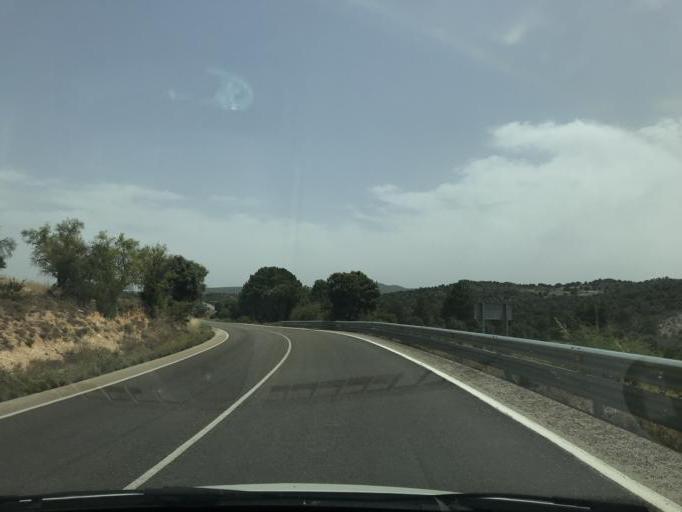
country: ES
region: Castille-La Mancha
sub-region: Provincia de Cuenca
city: Albalate de las Nogueras
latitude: 40.3946
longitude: -2.2578
